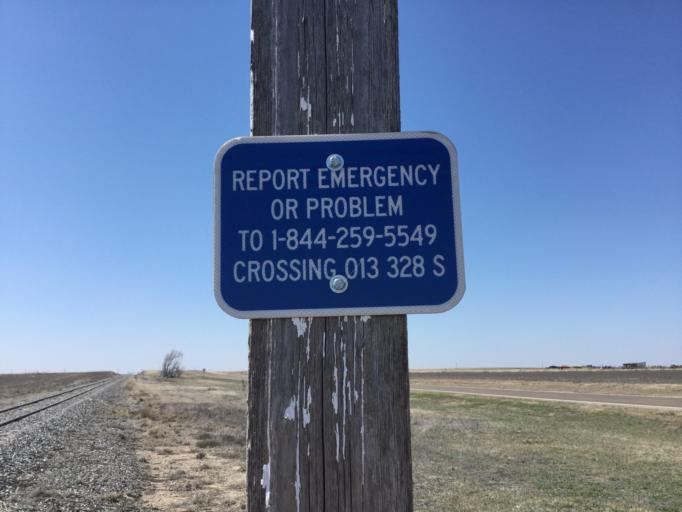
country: US
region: Kansas
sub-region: Stanton County
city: Johnson
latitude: 37.5571
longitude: -101.7801
